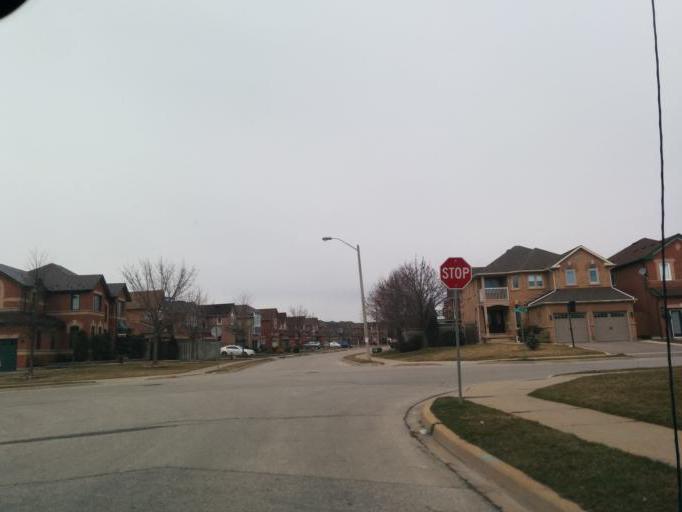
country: CA
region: Ontario
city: Brampton
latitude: 43.7280
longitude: -79.8231
